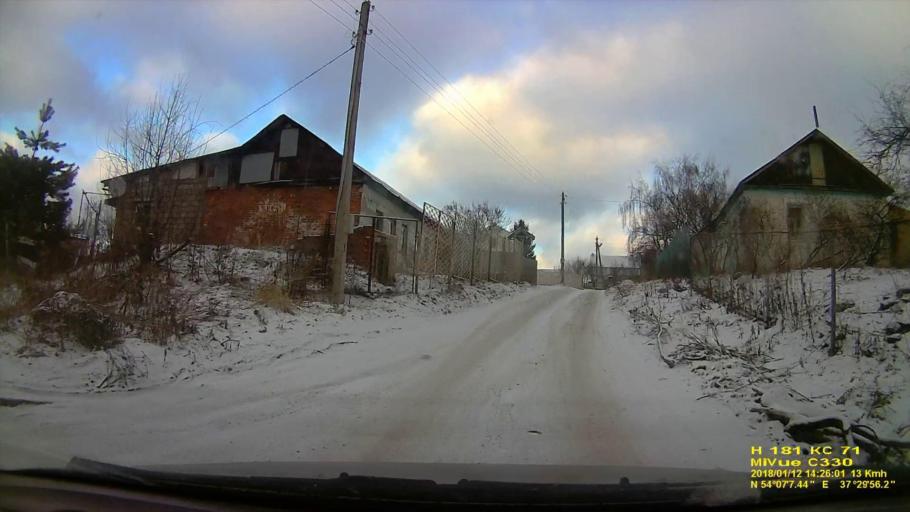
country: RU
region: Tula
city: Kosaya Gora
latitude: 54.1187
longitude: 37.4989
